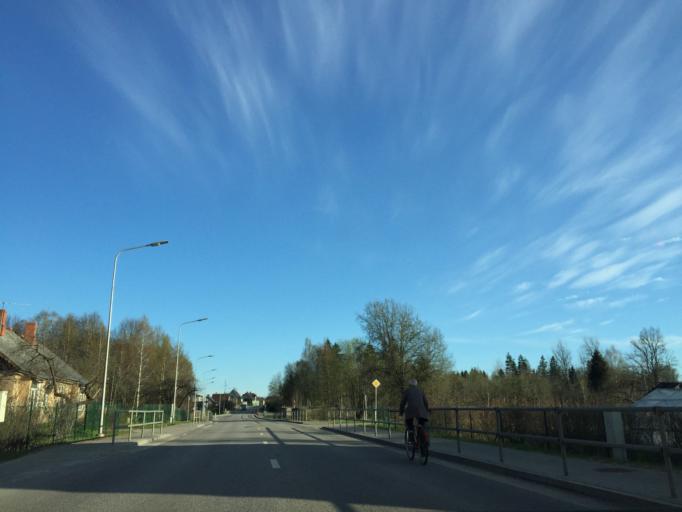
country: LV
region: Valkas Rajons
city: Valka
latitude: 57.7791
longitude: 25.9922
